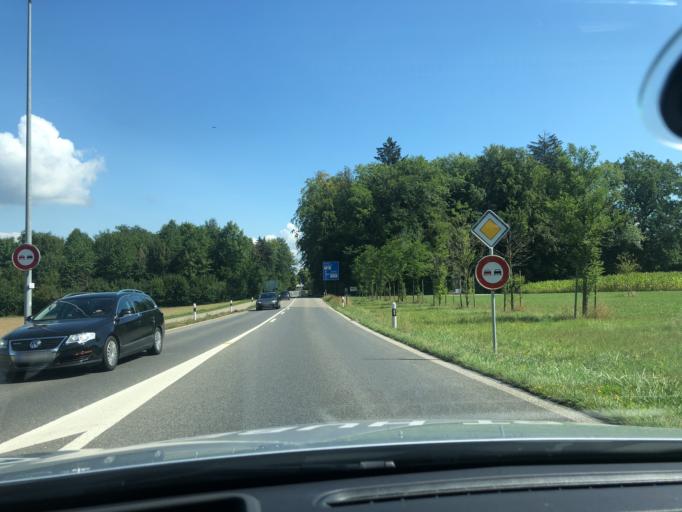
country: CH
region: Thurgau
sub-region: Kreuzlingen District
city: Tagerwilen
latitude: 47.6334
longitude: 9.1523
